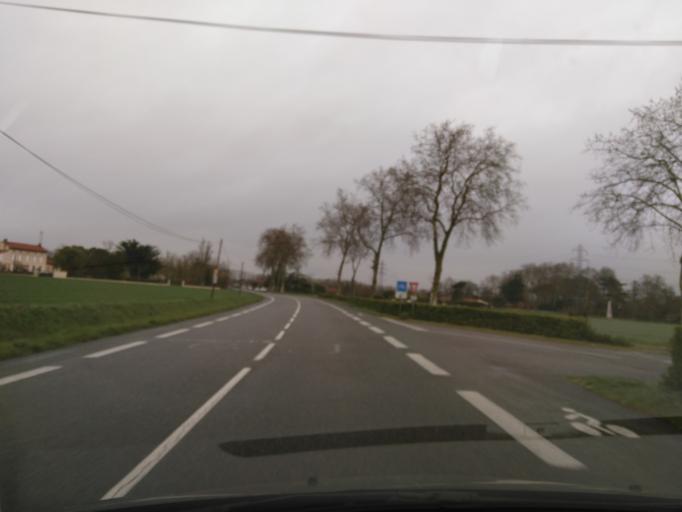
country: FR
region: Midi-Pyrenees
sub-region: Departement de la Haute-Garonne
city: Carbonne
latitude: 43.2851
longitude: 1.2168
